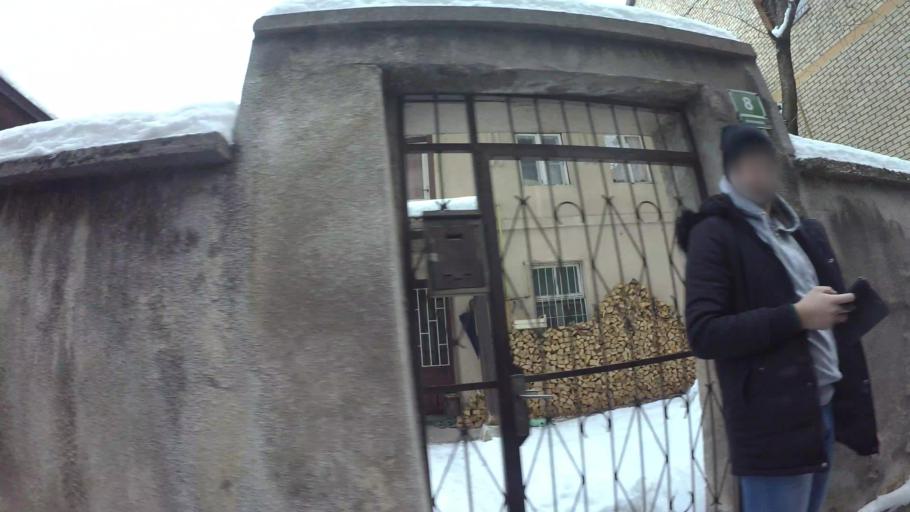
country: BA
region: Federation of Bosnia and Herzegovina
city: Kobilja Glava
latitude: 43.8613
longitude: 18.4244
